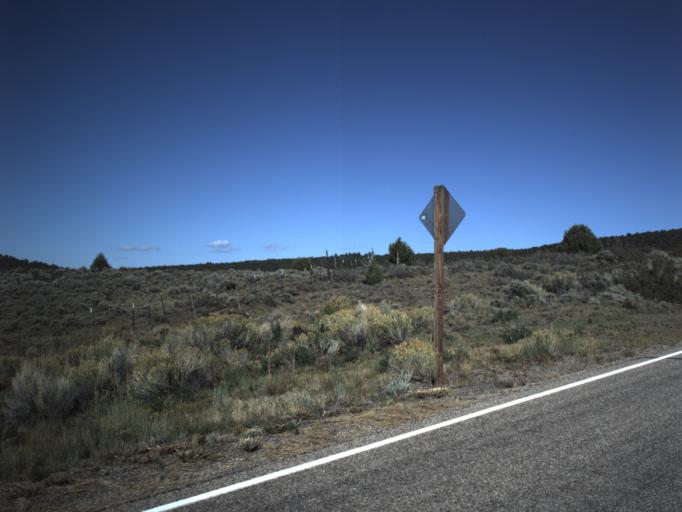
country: US
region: Utah
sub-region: Garfield County
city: Panguitch
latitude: 37.7673
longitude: -112.5439
